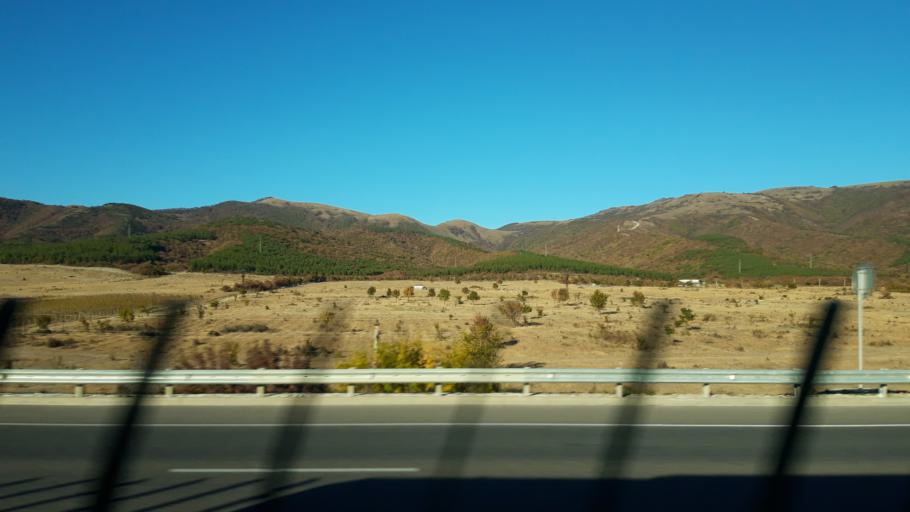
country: RU
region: Krasnodarskiy
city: Kabardinka
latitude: 44.6371
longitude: 37.9902
